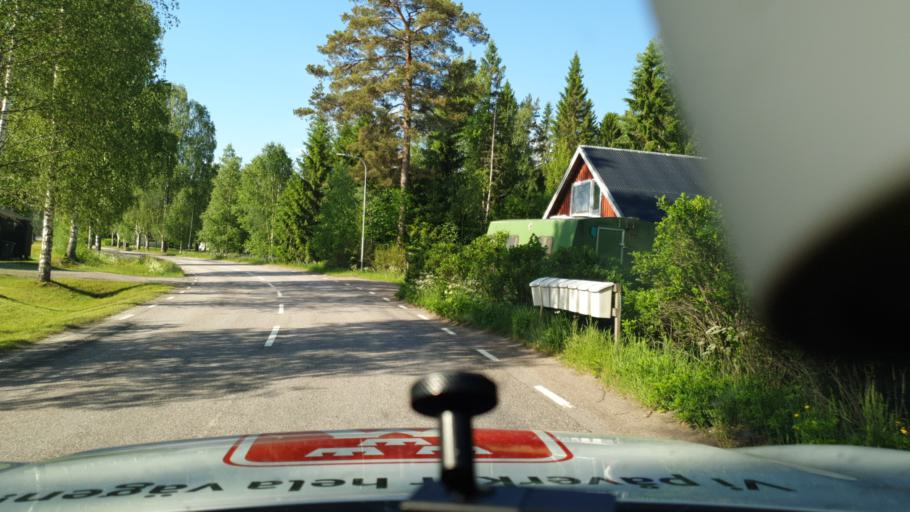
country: SE
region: Vaermland
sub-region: Torsby Kommun
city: Torsby
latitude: 59.9444
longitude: 12.9038
